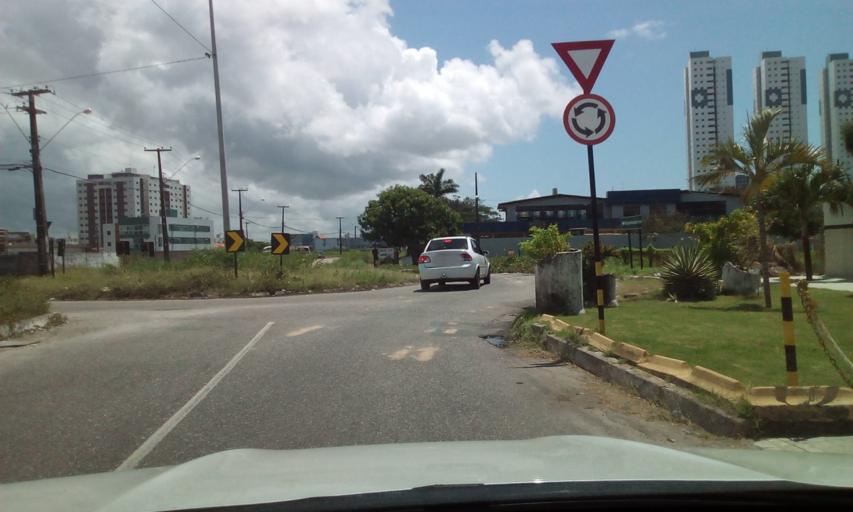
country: BR
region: Paraiba
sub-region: Joao Pessoa
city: Joao Pessoa
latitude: -7.0766
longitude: -34.8408
